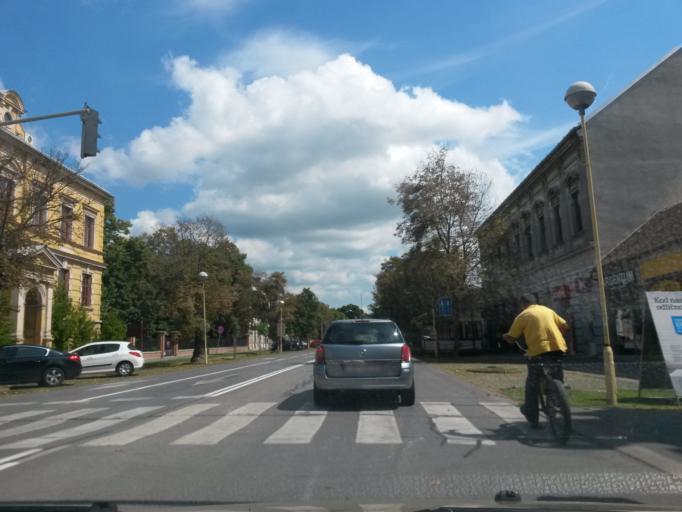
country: HR
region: Osjecko-Baranjska
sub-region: Grad Osijek
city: Osijek
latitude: 45.5582
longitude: 18.6806
